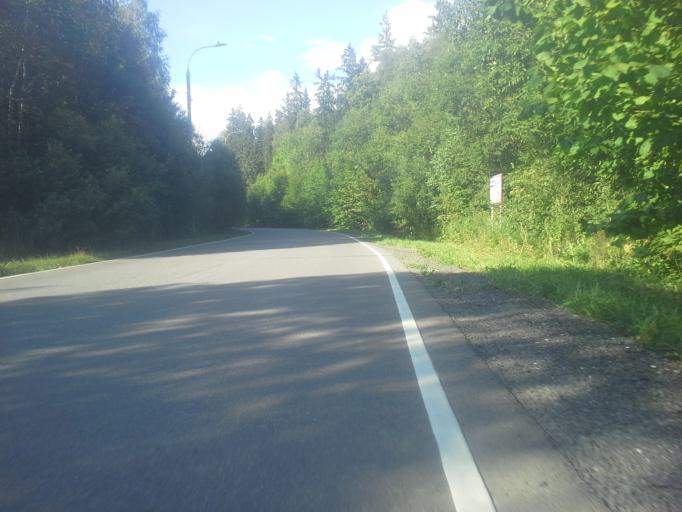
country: RU
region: Moskovskaya
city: Kievskij
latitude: 55.3778
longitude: 36.9803
